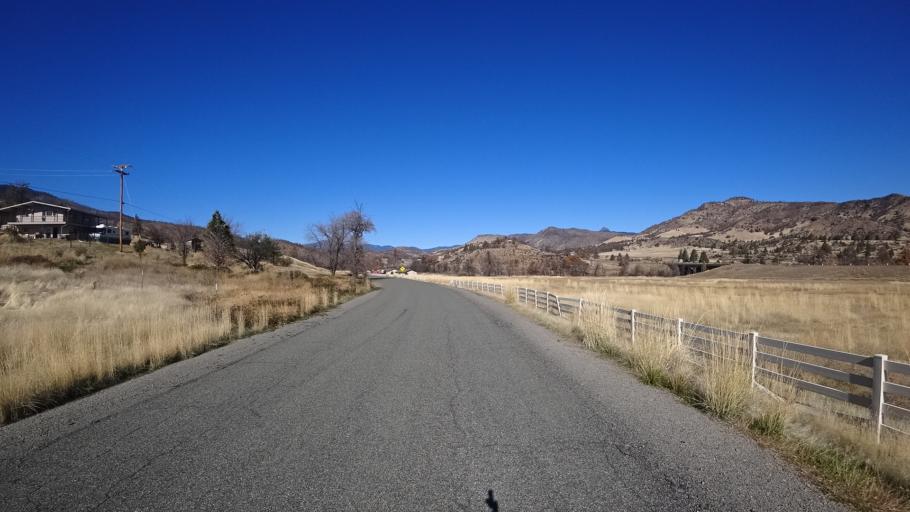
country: US
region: California
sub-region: Siskiyou County
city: Yreka
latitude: 41.9283
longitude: -122.5837
